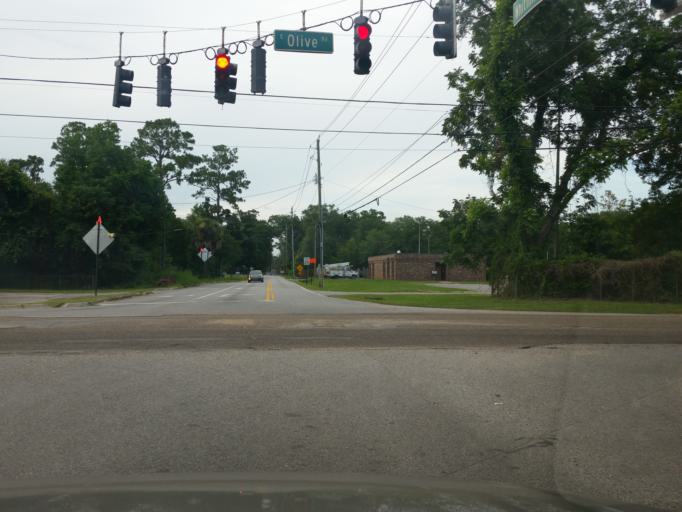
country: US
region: Florida
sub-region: Escambia County
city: Ferry Pass
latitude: 30.5105
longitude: -87.2269
